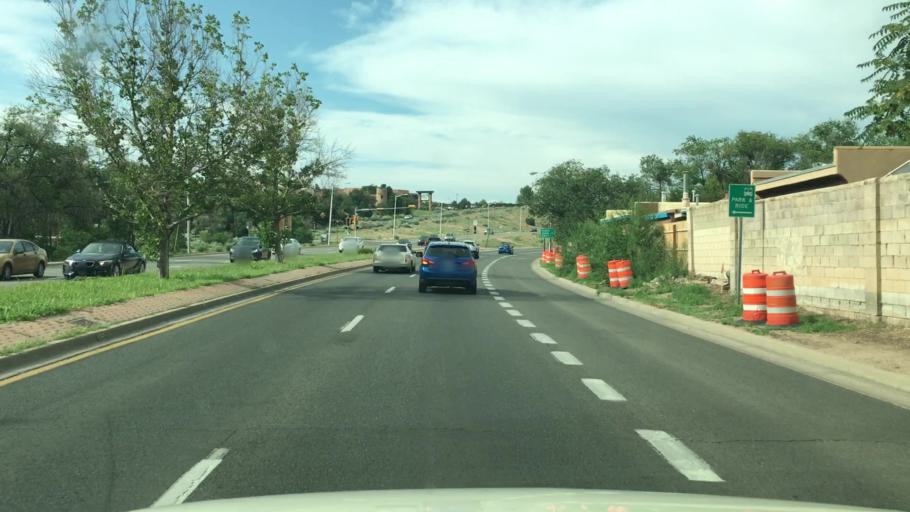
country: US
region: New Mexico
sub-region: Santa Fe County
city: Santa Fe
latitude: 35.6951
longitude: -105.9539
